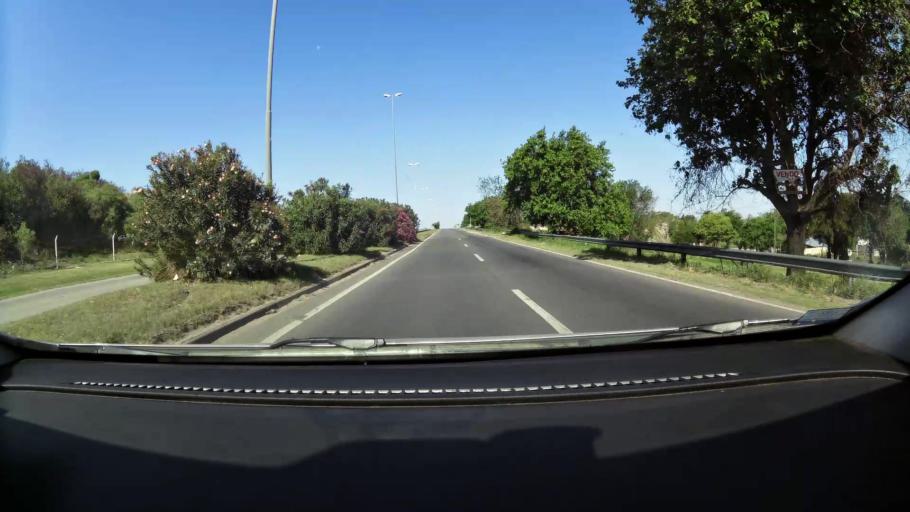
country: AR
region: Cordoba
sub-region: Departamento de Capital
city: Cordoba
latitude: -31.3982
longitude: -64.1342
